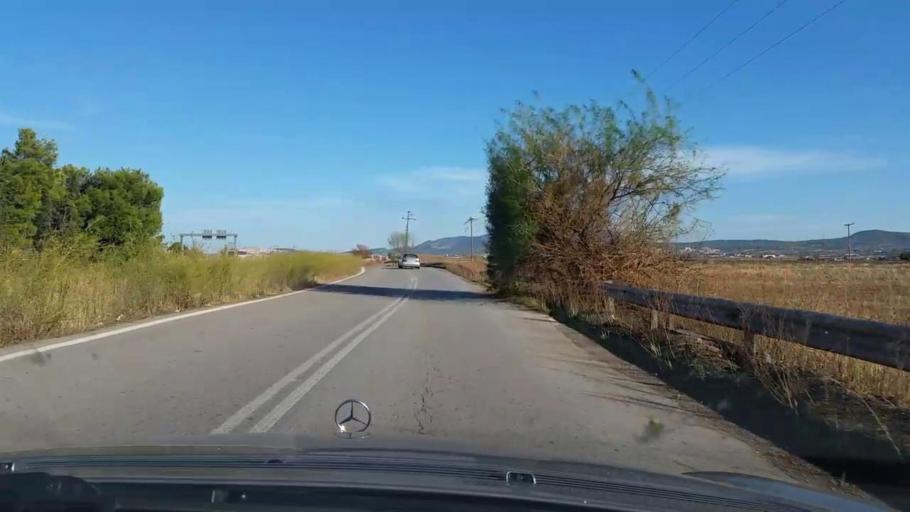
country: GR
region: Central Greece
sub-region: Nomos Voiotias
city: Thivai
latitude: 38.3700
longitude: 23.2885
